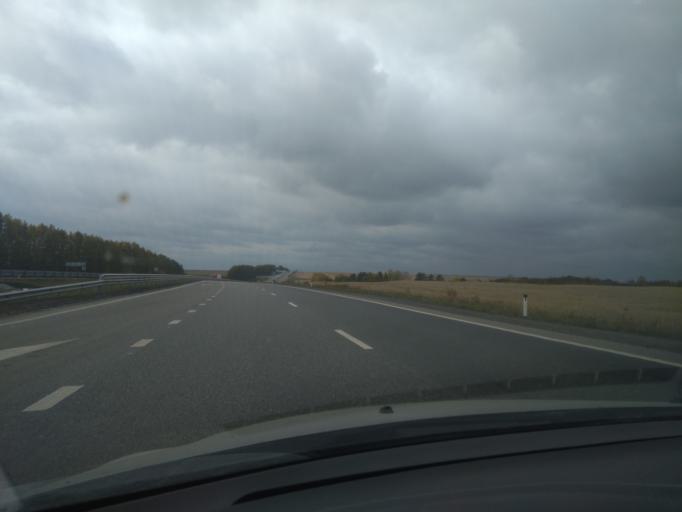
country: RU
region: Sverdlovsk
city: Kamyshlov
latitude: 56.8728
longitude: 62.9468
